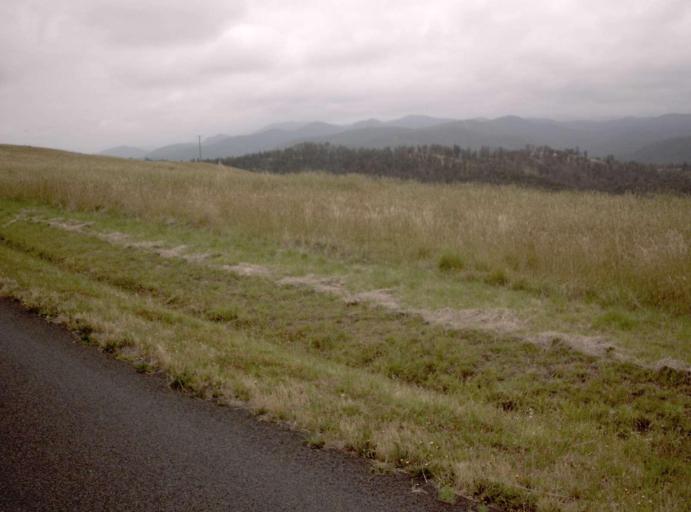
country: AU
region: Victoria
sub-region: Wellington
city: Heyfield
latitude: -37.8379
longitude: 146.6834
